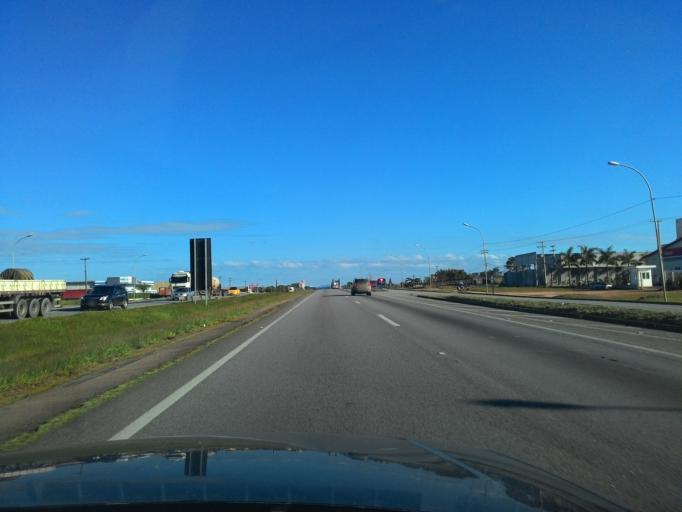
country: BR
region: Sao Paulo
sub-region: Registro
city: Registro
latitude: -24.5132
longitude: -47.8509
